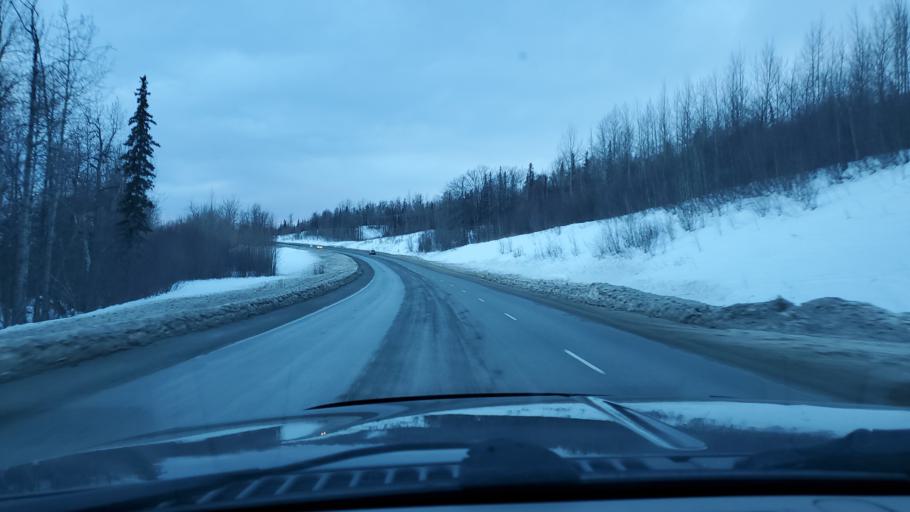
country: US
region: Alaska
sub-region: Matanuska-Susitna Borough
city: Lazy Mountain
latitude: 61.7112
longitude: -148.9184
